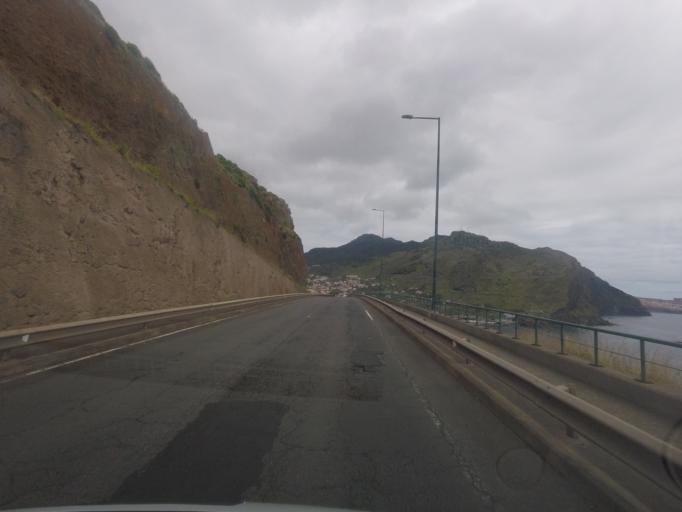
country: PT
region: Madeira
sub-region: Machico
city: Machico
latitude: 32.7110
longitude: -16.7618
